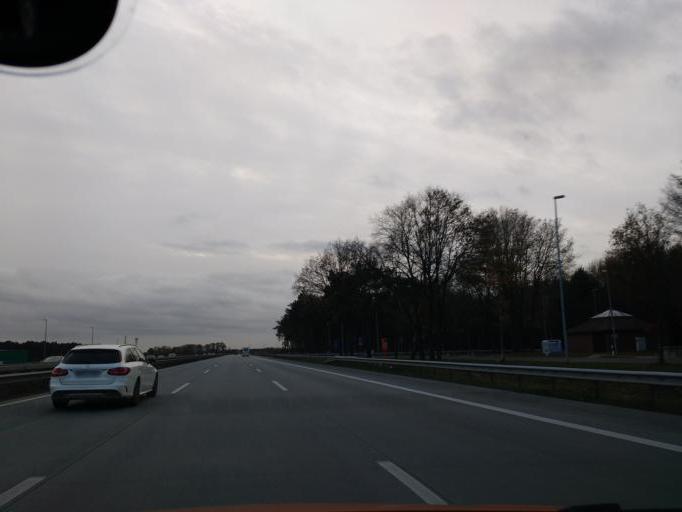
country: DE
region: Lower Saxony
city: Gross Meckelsen
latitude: 53.2553
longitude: 9.4287
